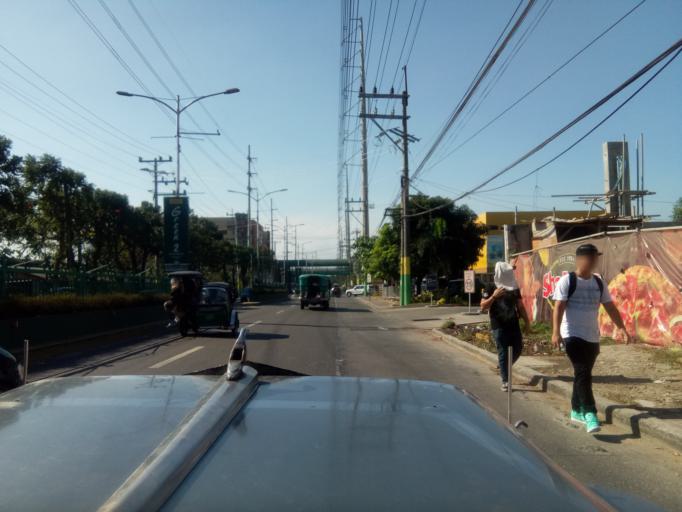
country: PH
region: Calabarzon
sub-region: Province of Cavite
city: Dasmarinas
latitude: 14.3240
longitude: 120.9412
